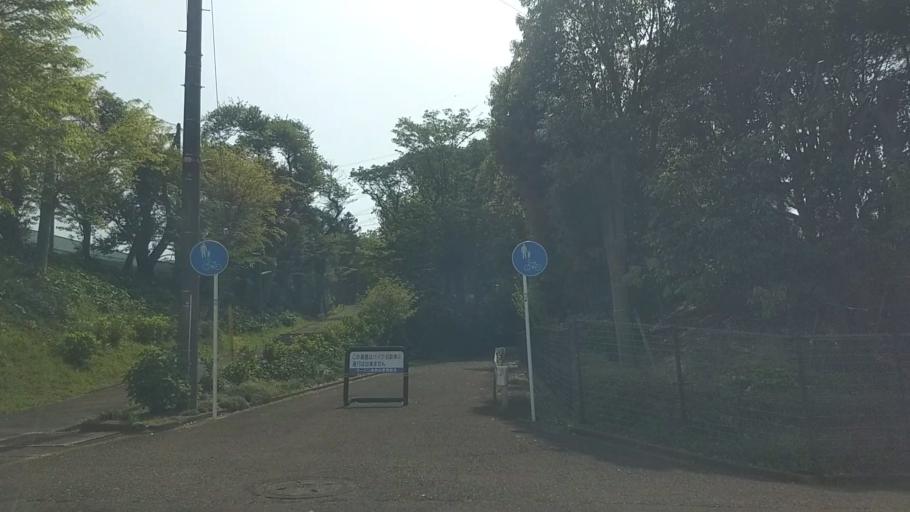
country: JP
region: Kanagawa
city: Kamakura
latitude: 35.3687
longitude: 139.5760
